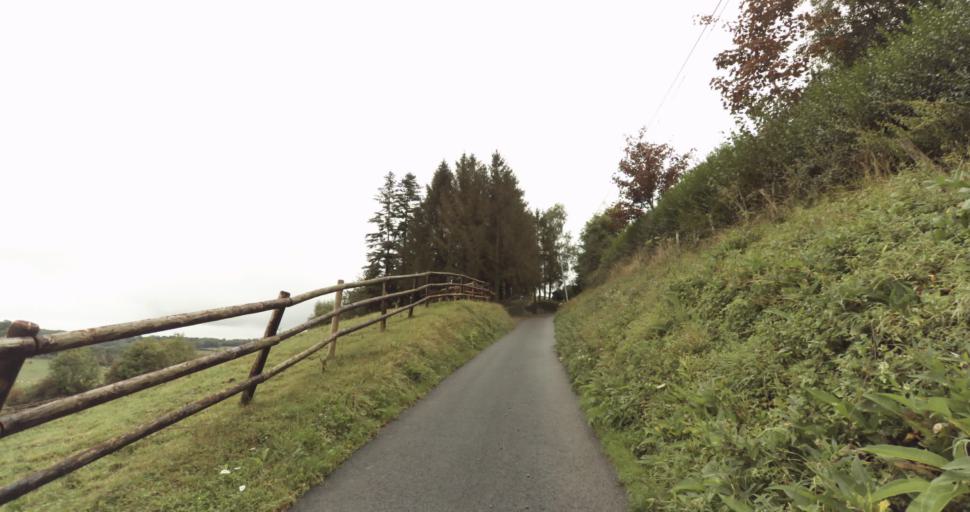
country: FR
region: Lower Normandy
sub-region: Departement de l'Orne
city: Vimoutiers
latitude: 48.8726
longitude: 0.2199
